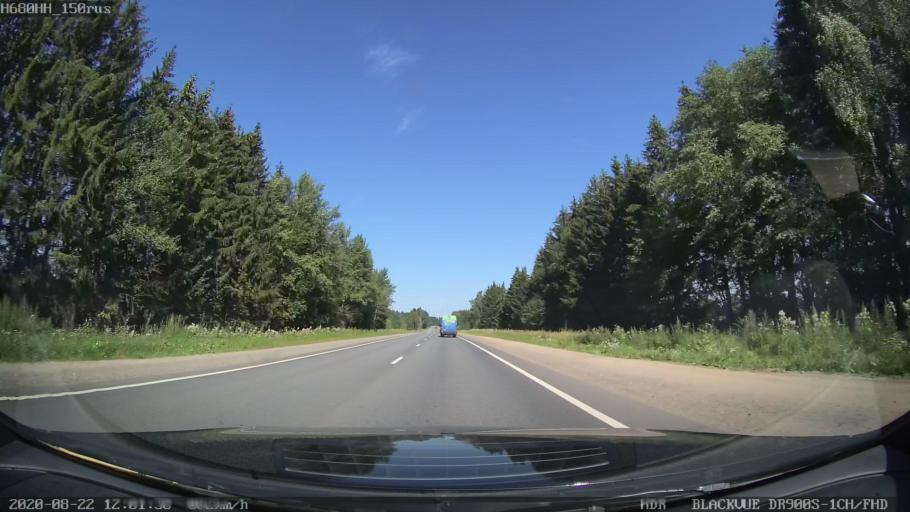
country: RU
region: Tverskaya
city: Rameshki
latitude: 57.2314
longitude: 36.1000
